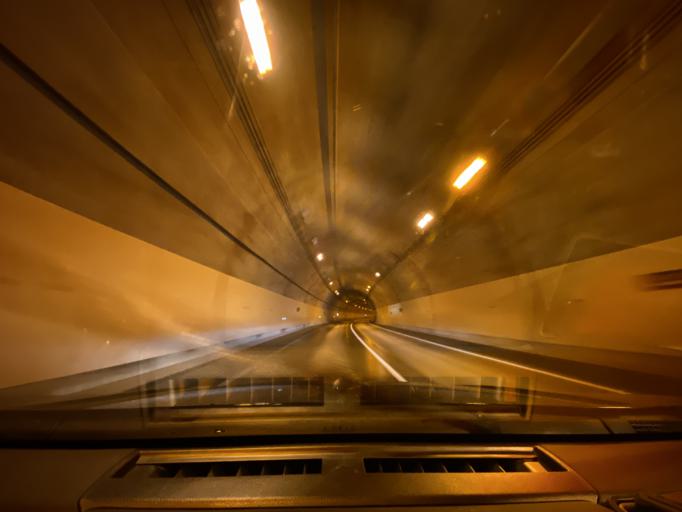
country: JP
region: Hokkaido
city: Rumoi
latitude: 43.8128
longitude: 141.4108
